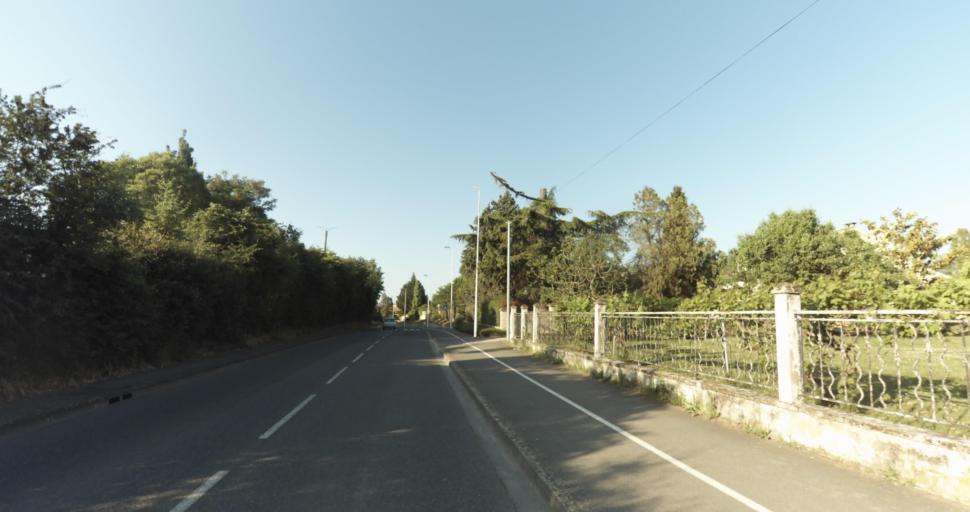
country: FR
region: Midi-Pyrenees
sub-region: Departement de la Haute-Garonne
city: Leguevin
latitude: 43.6044
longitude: 1.2335
